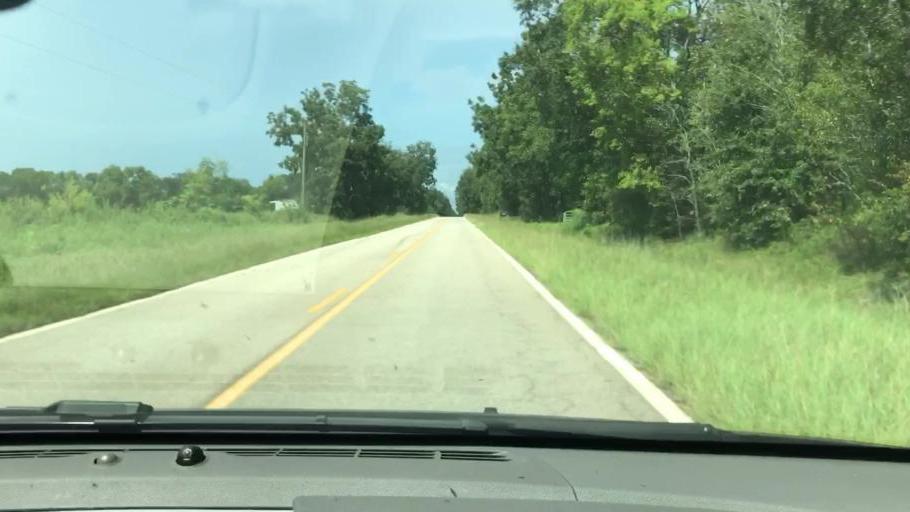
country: US
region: Georgia
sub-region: Seminole County
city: Donalsonville
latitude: 31.1320
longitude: -84.9953
